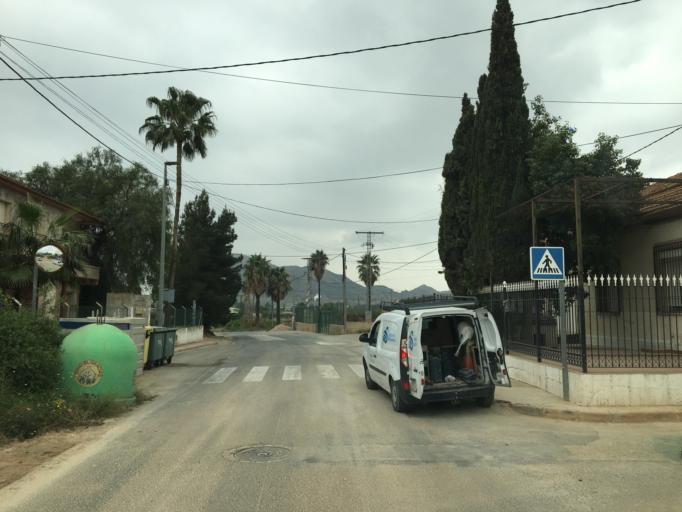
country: ES
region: Murcia
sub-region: Murcia
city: Santomera
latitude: 38.0755
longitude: -1.0416
